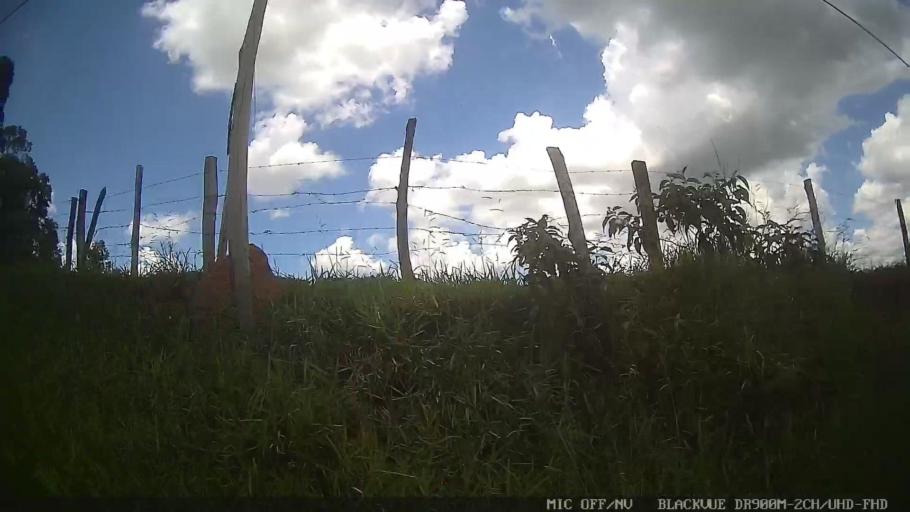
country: BR
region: Sao Paulo
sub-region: Braganca Paulista
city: Braganca Paulista
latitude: -22.9923
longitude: -46.4856
